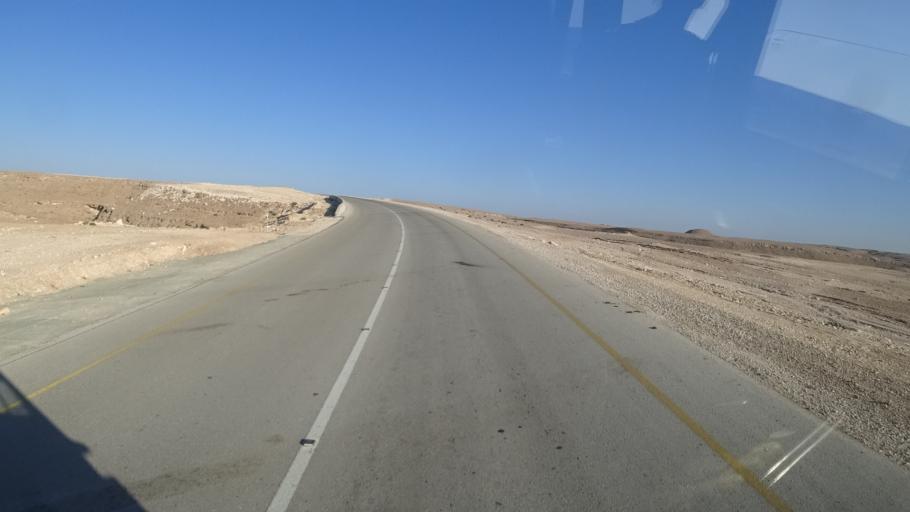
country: YE
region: Al Mahrah
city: Hawf
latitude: 17.0870
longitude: 53.0742
